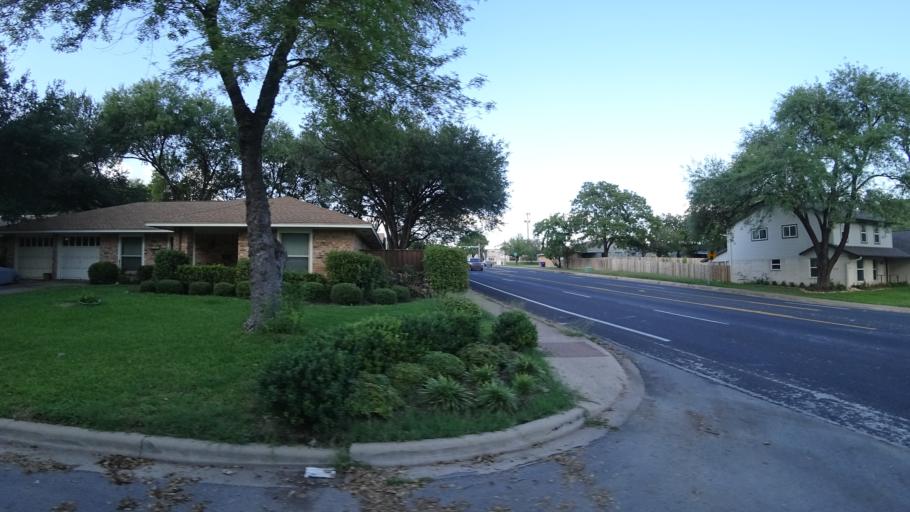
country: US
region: Texas
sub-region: Travis County
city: Wells Branch
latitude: 30.3667
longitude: -97.7068
